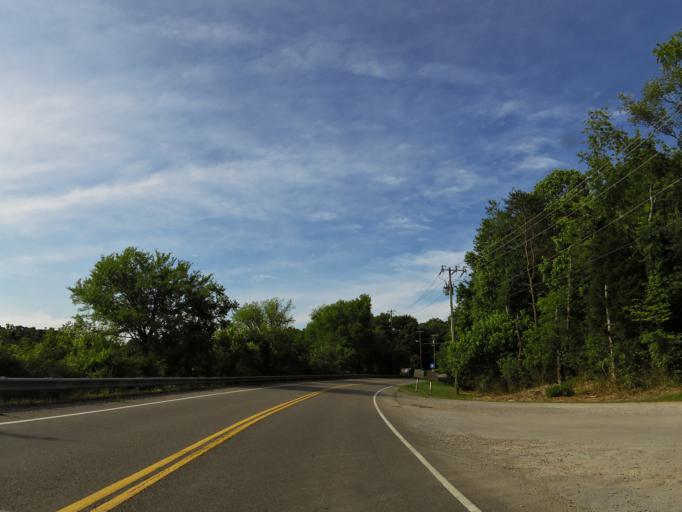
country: US
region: Tennessee
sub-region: Blount County
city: Eagleton Village
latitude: 35.8722
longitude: -83.9434
